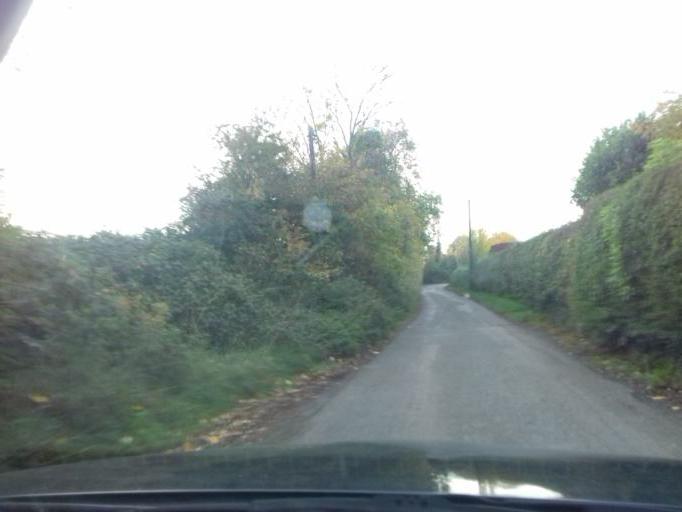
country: IE
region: Leinster
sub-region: An Mhi
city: Dunboyne
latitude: 53.3850
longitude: -6.4596
